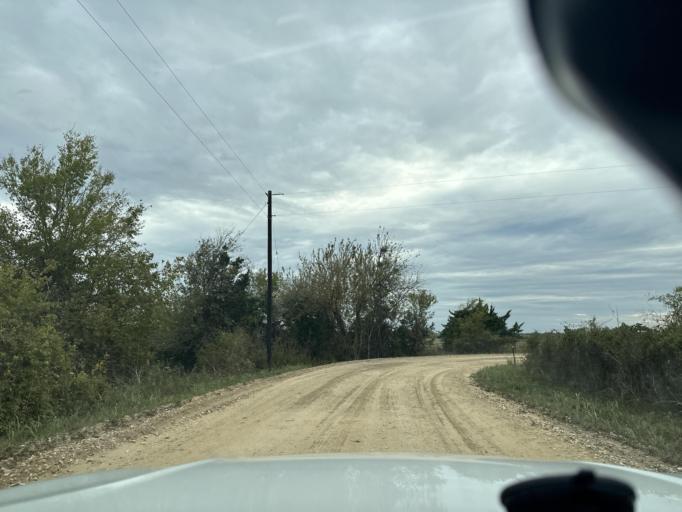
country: US
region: Texas
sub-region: Burleson County
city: Somerville
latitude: 30.1650
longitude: -96.6422
